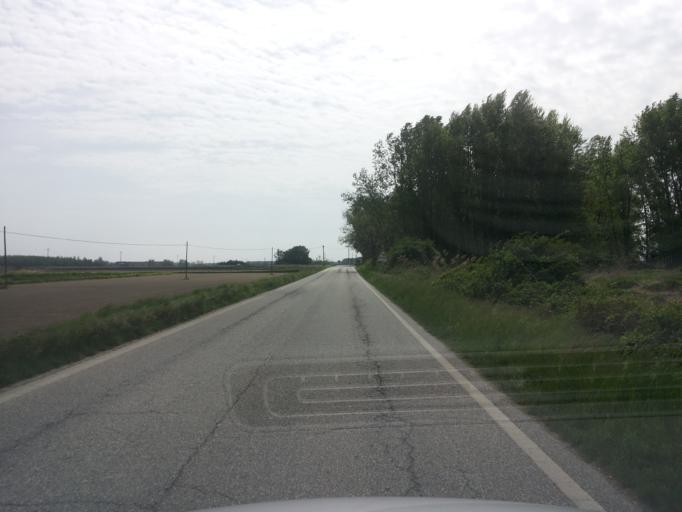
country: IT
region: Piedmont
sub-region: Provincia di Vercelli
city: Caresana
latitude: 45.2109
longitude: 8.5071
